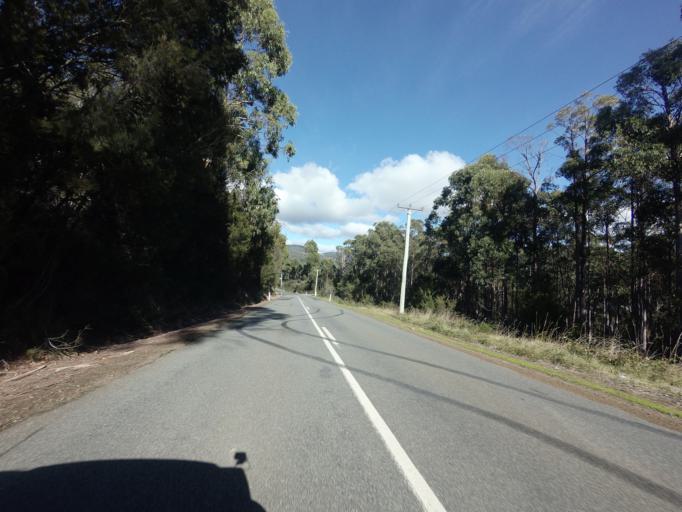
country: AU
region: Tasmania
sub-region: Clarence
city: Sandford
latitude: -43.0588
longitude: 147.8453
